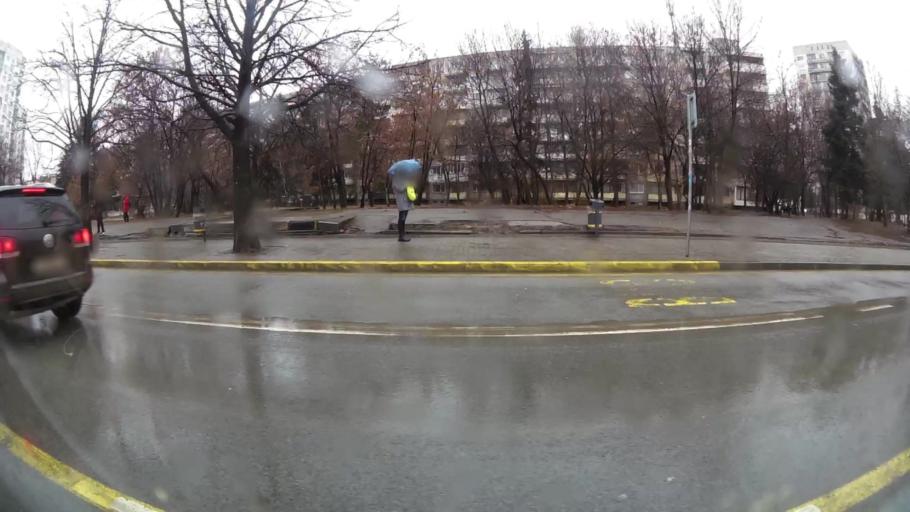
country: BG
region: Sofia-Capital
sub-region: Stolichna Obshtina
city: Sofia
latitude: 42.6519
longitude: 23.3792
